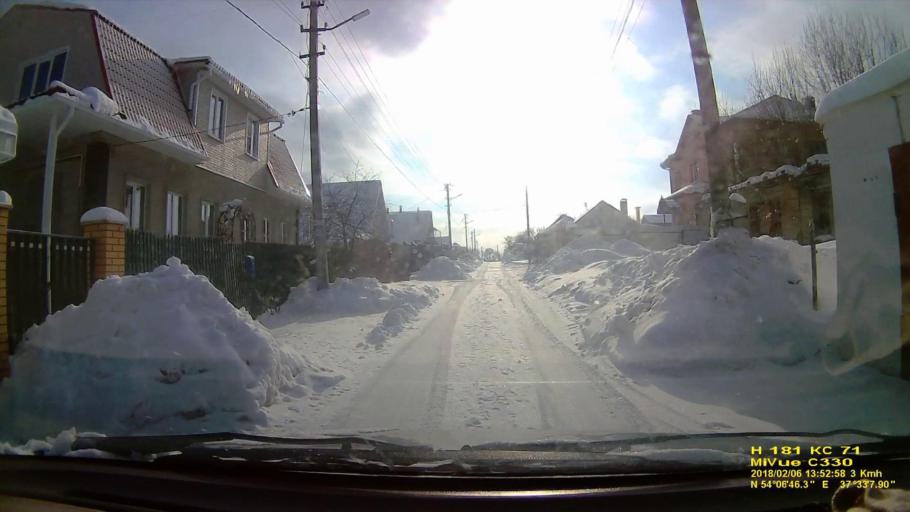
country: RU
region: Tula
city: Kosaya Gora
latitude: 54.1128
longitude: 37.5522
